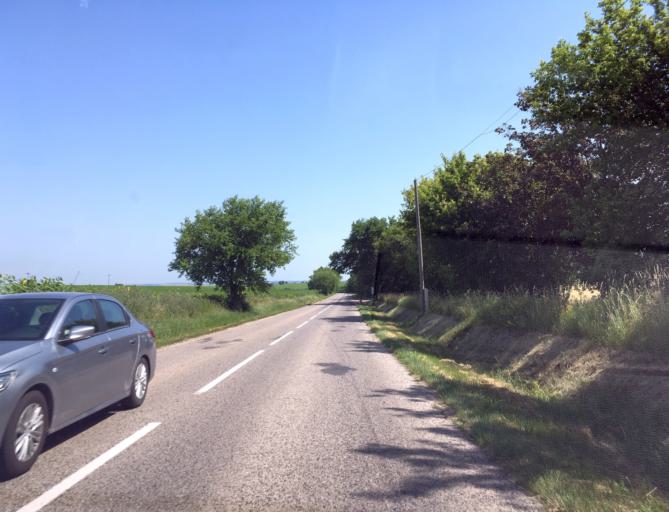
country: SK
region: Nitriansky
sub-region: Okres Komarno
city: Hurbanovo
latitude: 47.8729
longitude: 18.2830
